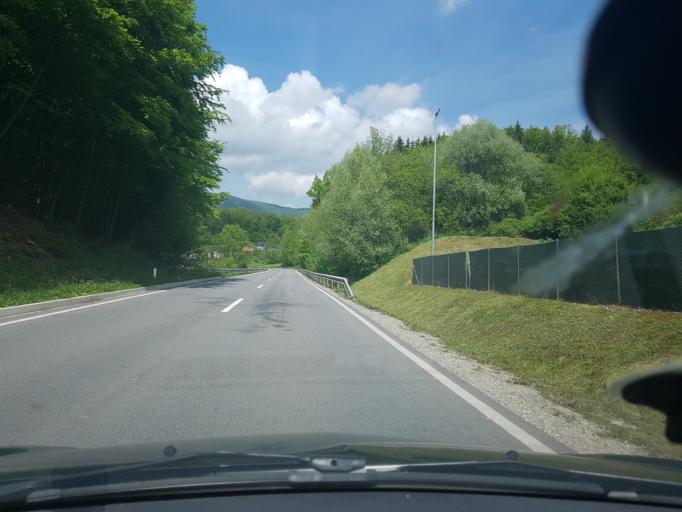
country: SI
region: Rogatec
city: Rogatec
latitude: 46.2373
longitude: 15.6712
